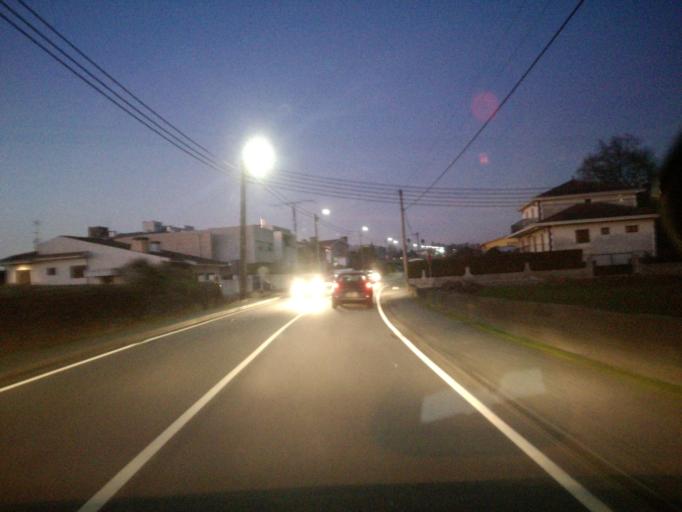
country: PT
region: Porto
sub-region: Maia
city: Nogueira
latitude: 41.2464
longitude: -8.5858
